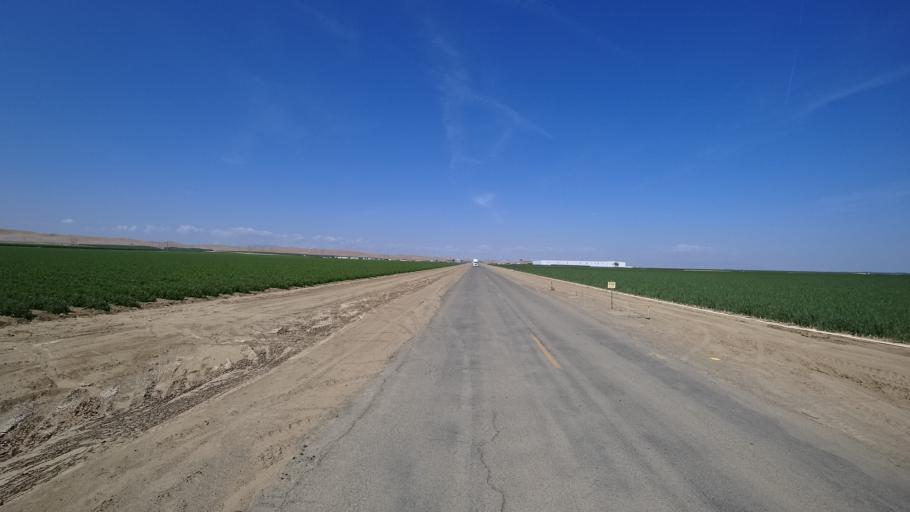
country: US
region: California
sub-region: Kings County
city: Kettleman City
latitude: 36.0724
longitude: -120.0396
